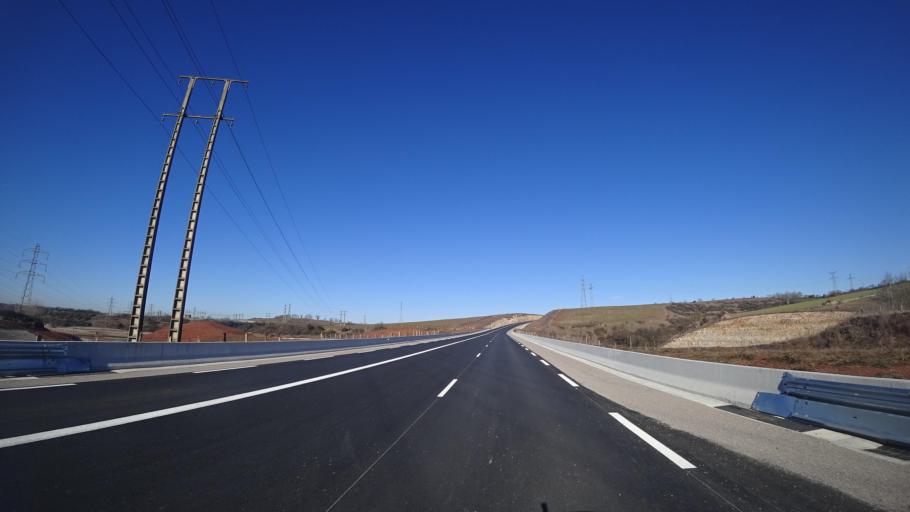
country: FR
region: Midi-Pyrenees
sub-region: Departement de l'Aveyron
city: Sebazac-Concoures
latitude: 44.3850
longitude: 2.6155
